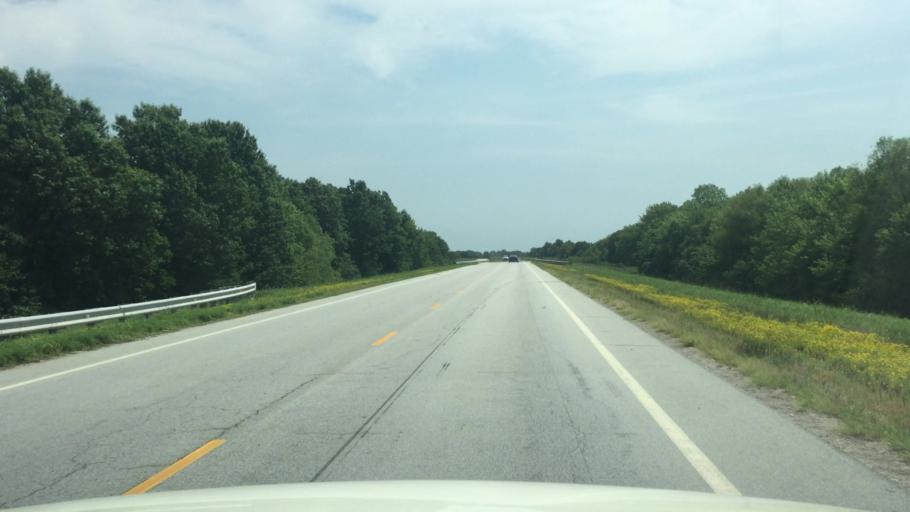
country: US
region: Kansas
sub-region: Cherokee County
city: Columbus
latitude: 37.1801
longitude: -94.9761
